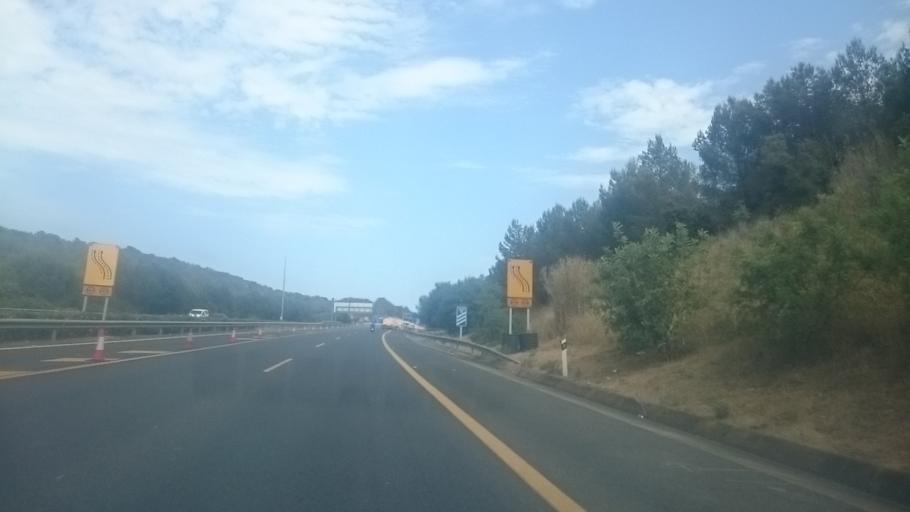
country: ES
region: Catalonia
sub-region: Provincia de Barcelona
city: Sitges
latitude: 41.2524
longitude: 1.7970
